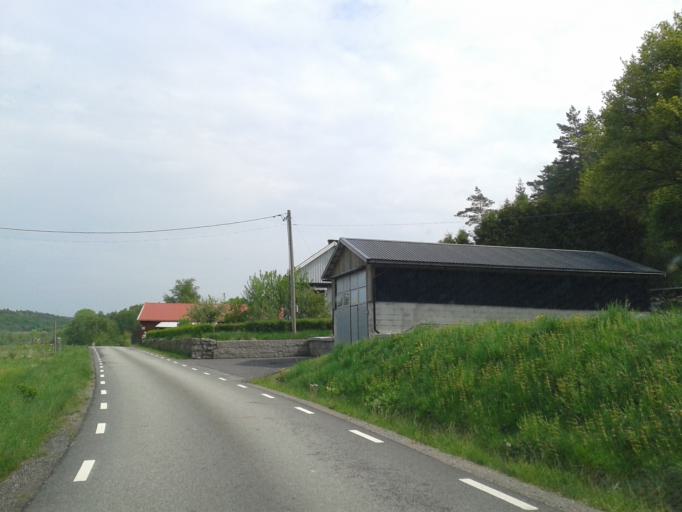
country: SE
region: Vaestra Goetaland
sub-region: Kungalvs Kommun
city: Diserod
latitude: 57.9222
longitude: 11.9640
